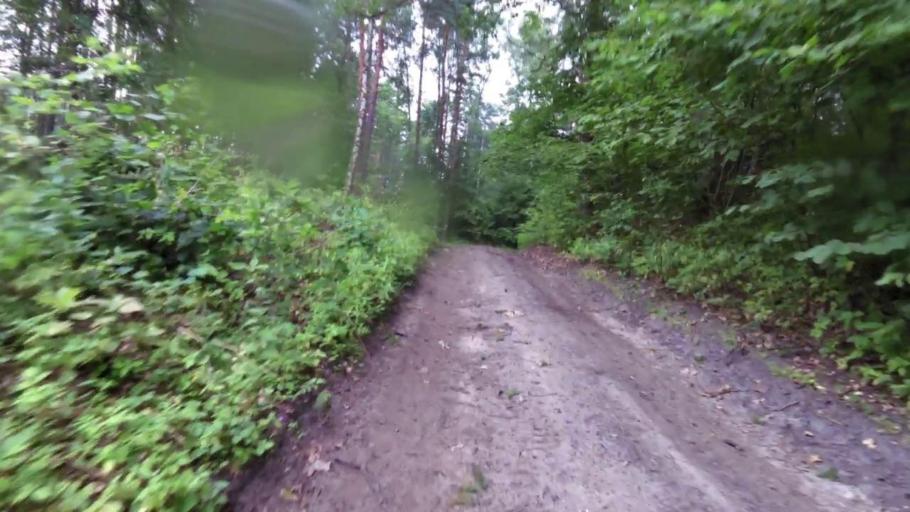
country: PL
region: West Pomeranian Voivodeship
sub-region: Powiat drawski
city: Drawsko Pomorskie
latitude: 53.5401
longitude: 15.6997
